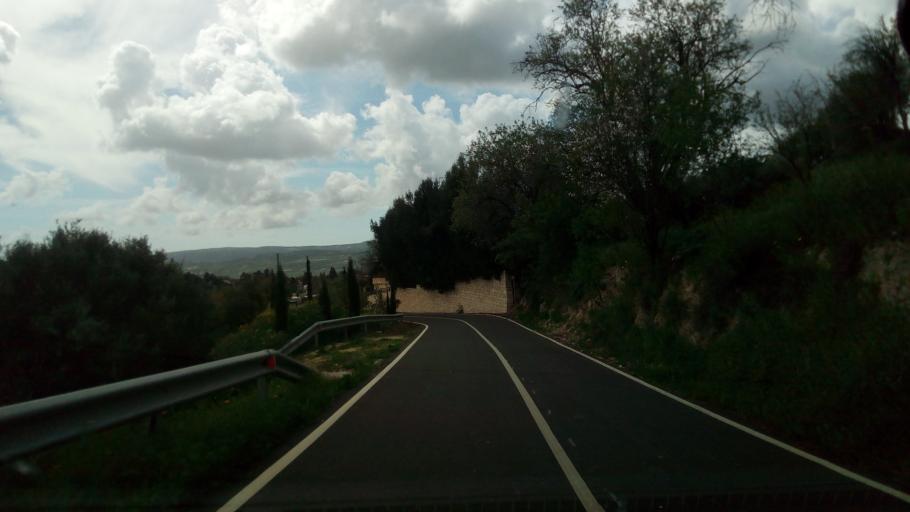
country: CY
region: Pafos
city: Mesogi
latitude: 34.8746
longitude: 32.5618
